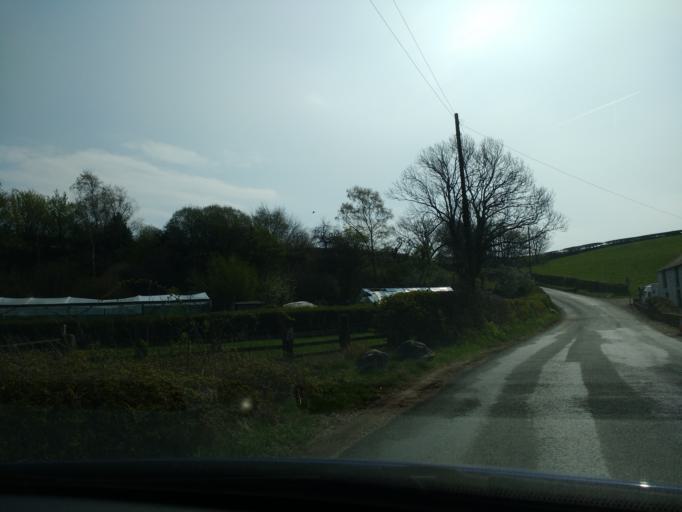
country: GB
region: England
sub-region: Lancashire
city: Bolton le Sands
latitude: 54.0852
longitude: -2.7955
